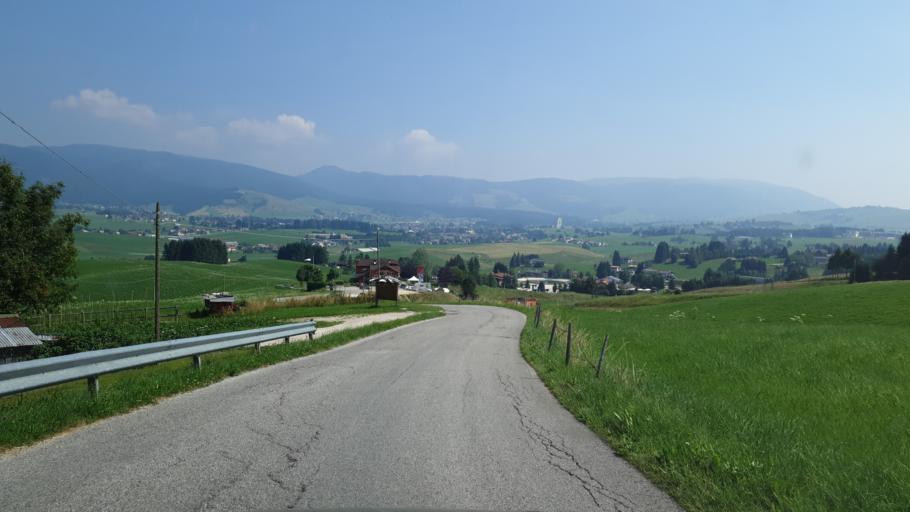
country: IT
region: Veneto
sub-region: Provincia di Vicenza
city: Canove di Roana
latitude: 45.8504
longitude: 11.4936
